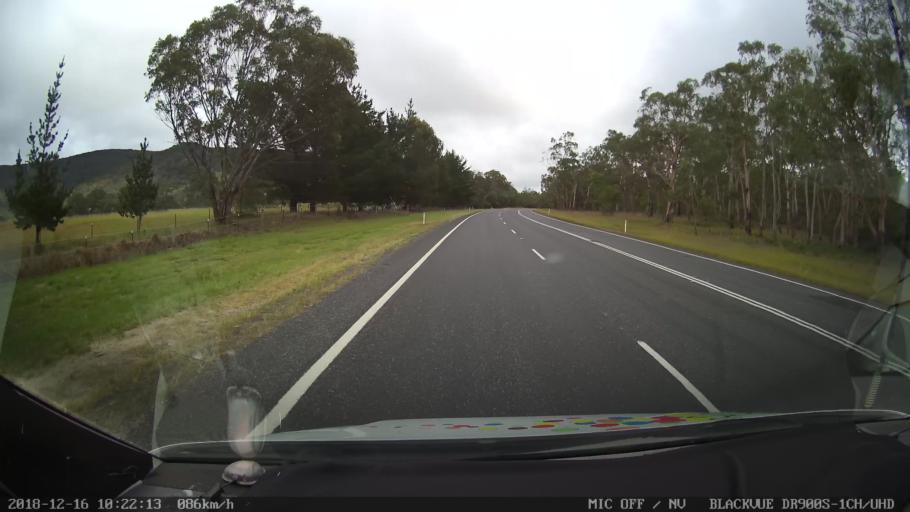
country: AU
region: New South Wales
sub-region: Tenterfield Municipality
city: Carrolls Creek
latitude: -29.1978
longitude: 152.0100
